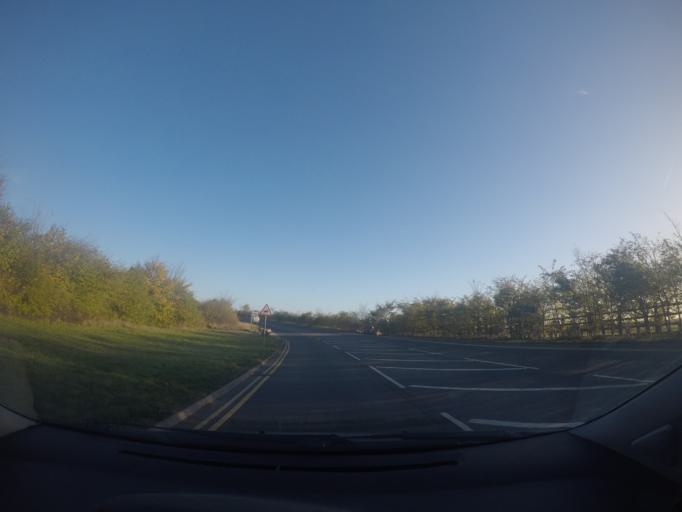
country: GB
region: England
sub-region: City of York
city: Askham Richard
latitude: 53.9049
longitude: -1.1844
